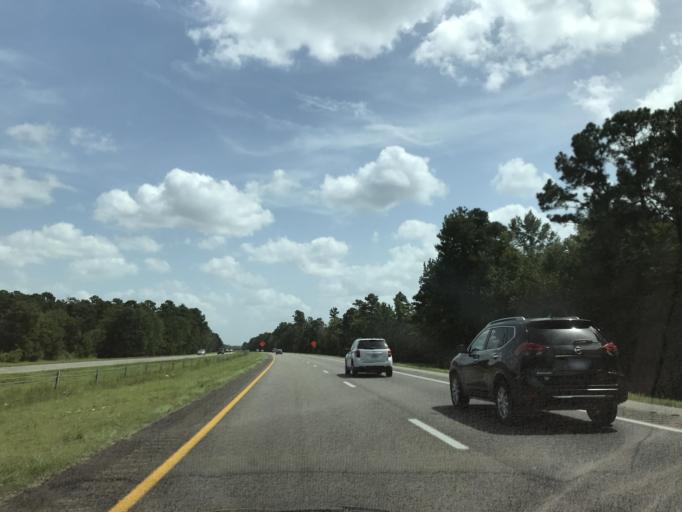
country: US
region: North Carolina
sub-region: Pender County
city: Burgaw
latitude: 34.6243
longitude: -77.9328
